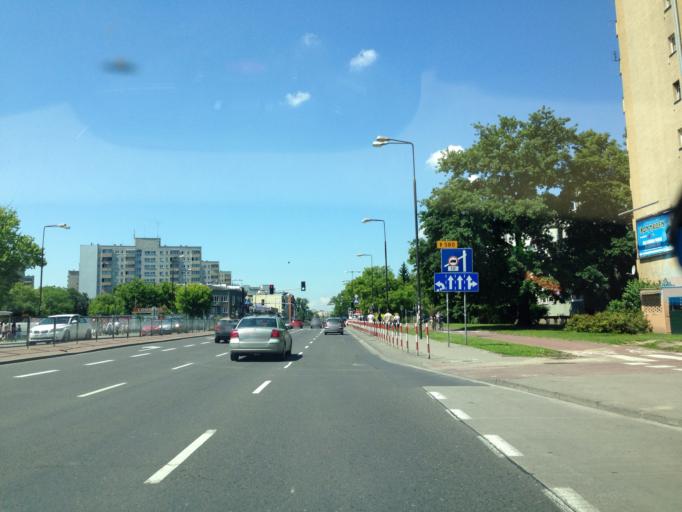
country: PL
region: Masovian Voivodeship
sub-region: Warszawa
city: Bemowo
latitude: 52.2392
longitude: 20.9444
